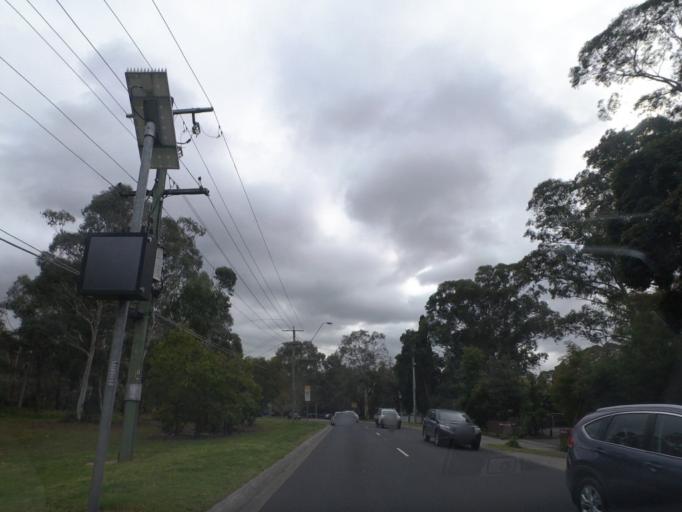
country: AU
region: Victoria
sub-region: Nillumbik
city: Eltham
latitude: -37.7265
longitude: 145.1470
